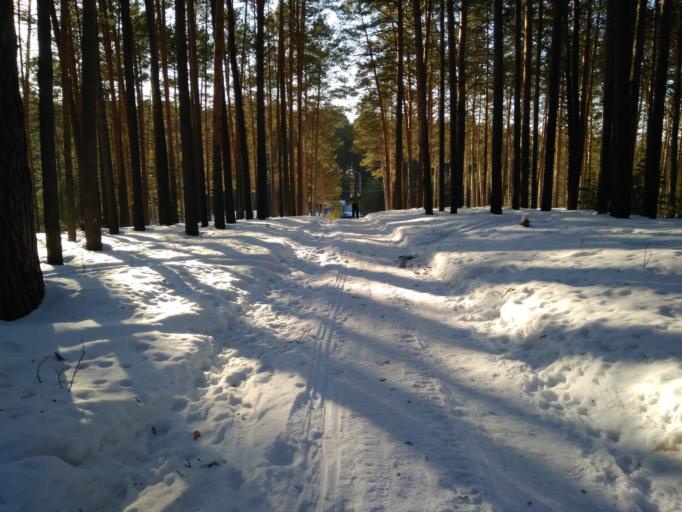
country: RU
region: Tomsk
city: Timiryazevskoye
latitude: 56.4834
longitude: 84.8732
